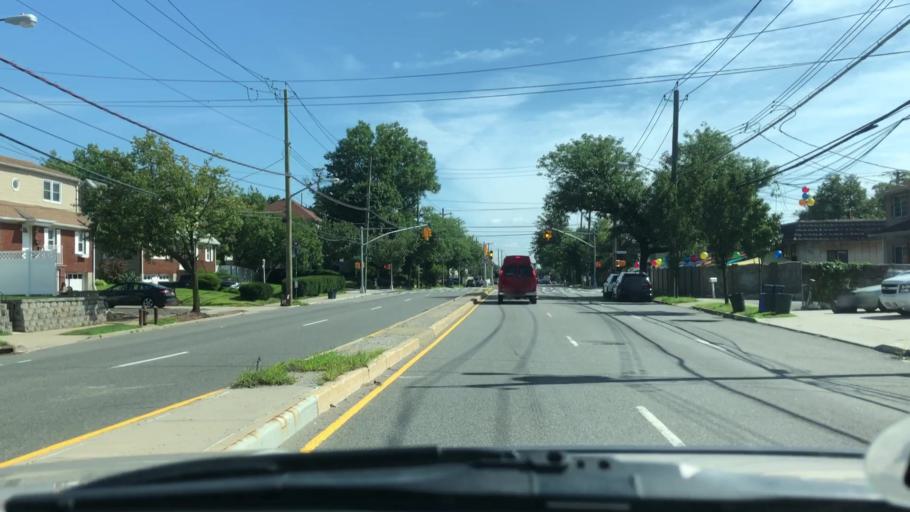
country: US
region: New York
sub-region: Richmond County
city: Staten Island
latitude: 40.5449
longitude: -74.1434
